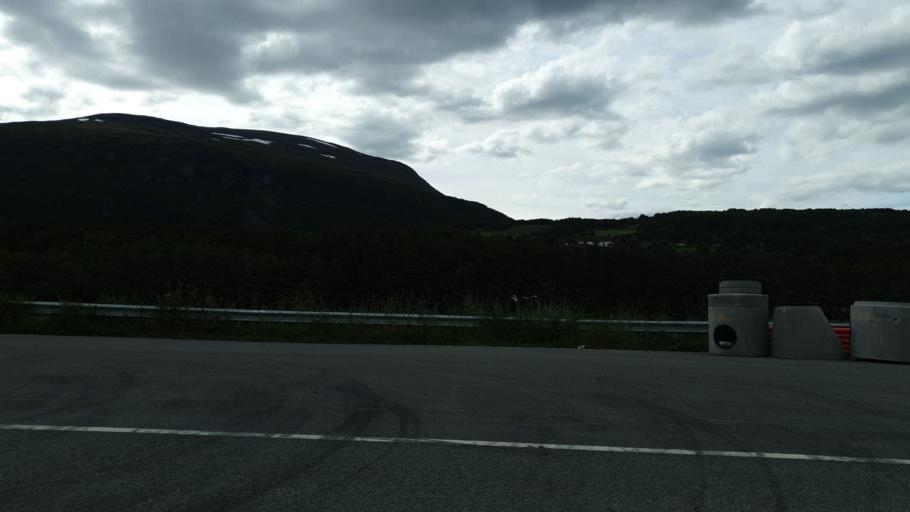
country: NO
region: Sor-Trondelag
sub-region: Oppdal
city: Oppdal
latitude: 62.5537
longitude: 9.6330
